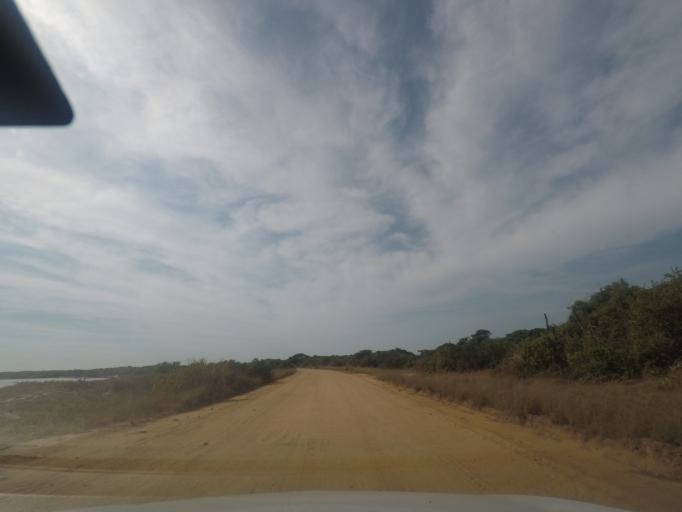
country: BR
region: Rio de Janeiro
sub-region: Marica
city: Marica
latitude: -22.9554
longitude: -42.8849
